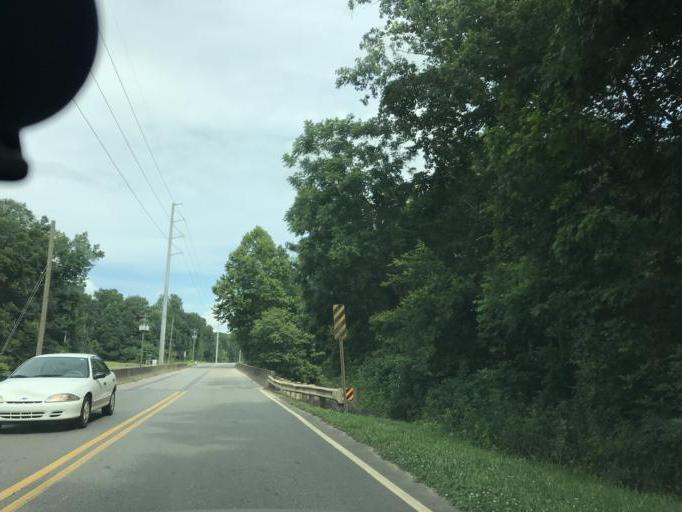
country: US
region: Georgia
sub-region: Forsyth County
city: Cumming
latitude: 34.3087
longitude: -84.2220
